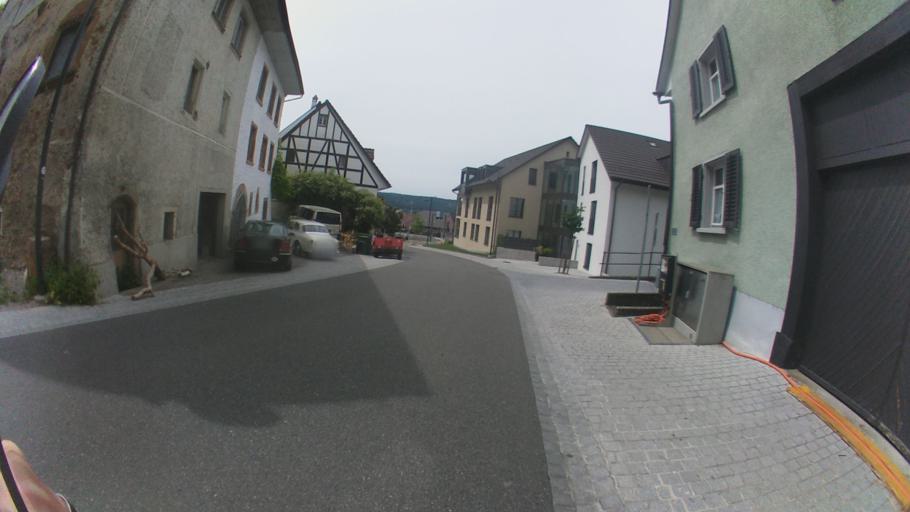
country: CH
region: Aargau
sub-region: Bezirk Zurzach
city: Klingnau
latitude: 47.5708
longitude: 8.2591
